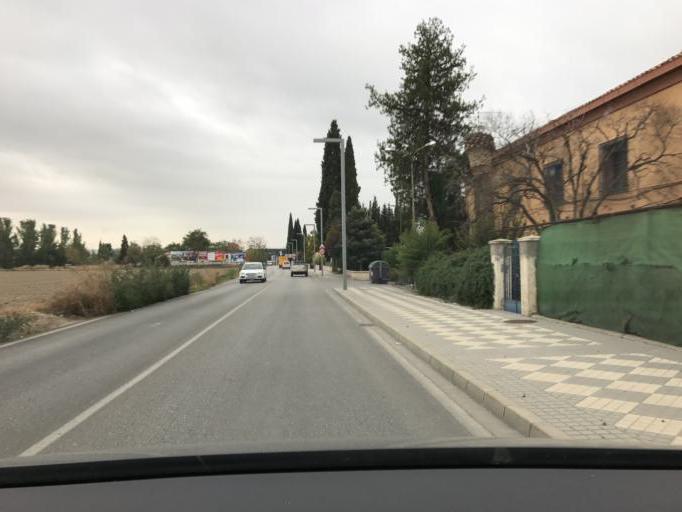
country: ES
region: Andalusia
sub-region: Provincia de Granada
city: Maracena
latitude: 37.2006
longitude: -3.6438
